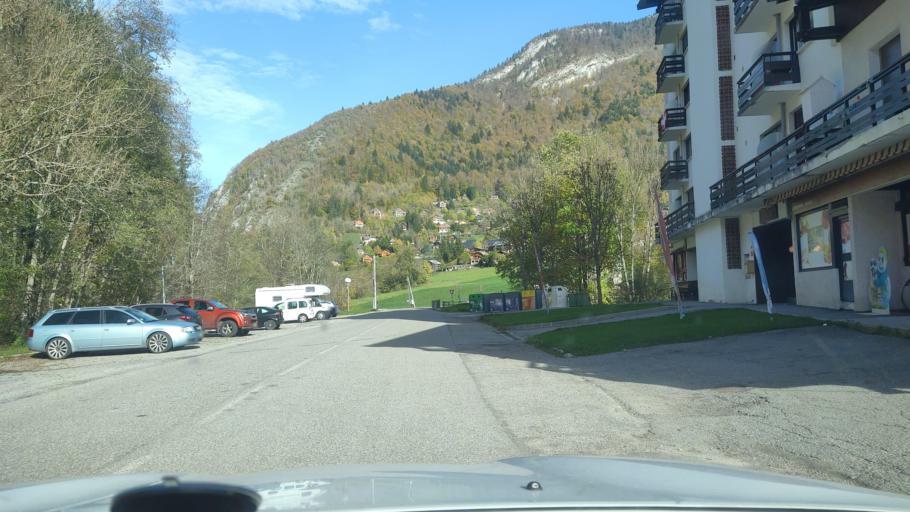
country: FR
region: Rhone-Alpes
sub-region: Departement de la Savoie
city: Cruet
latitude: 45.6072
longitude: 6.0990
